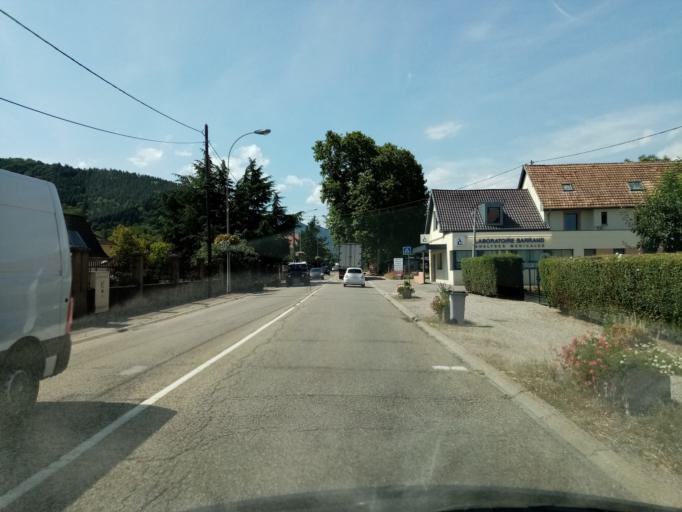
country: FR
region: Alsace
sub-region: Departement du Bas-Rhin
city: Chatenois
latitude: 48.2750
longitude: 7.4053
